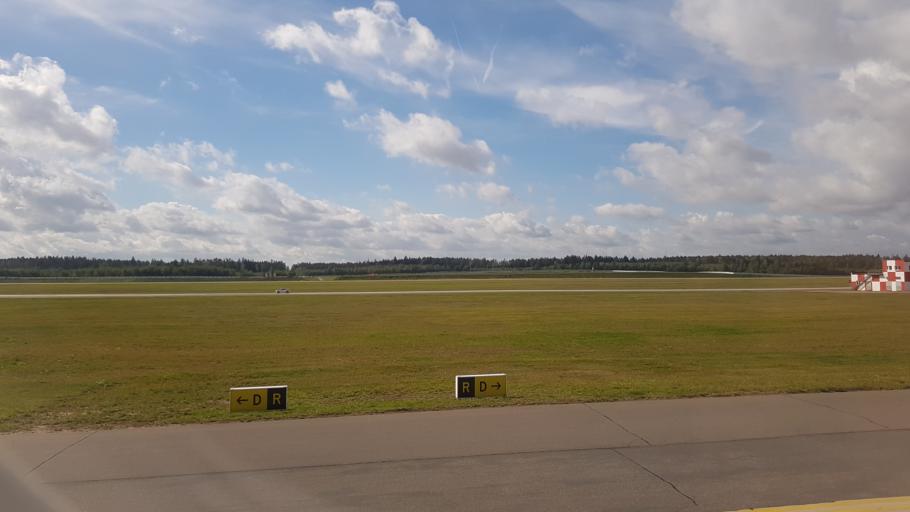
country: BY
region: Minsk
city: Smilavichy
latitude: 53.8867
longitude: 28.0327
